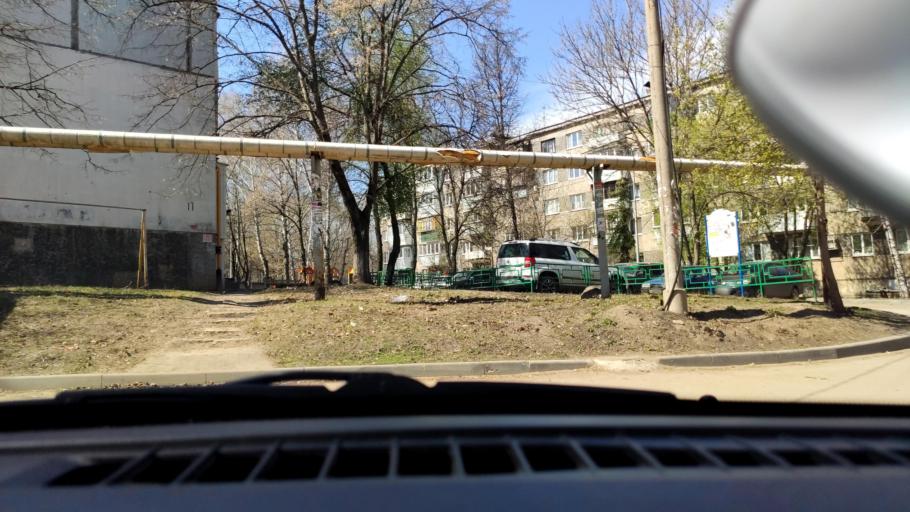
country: RU
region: Samara
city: Petra-Dubrava
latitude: 53.3048
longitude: 50.2738
